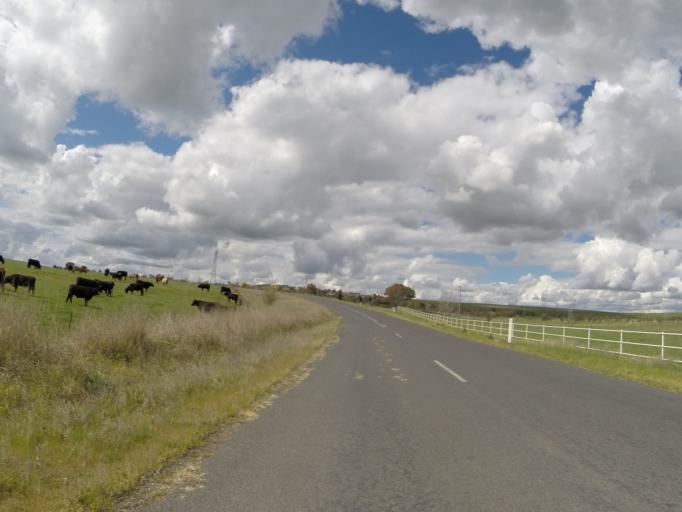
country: AU
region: New South Wales
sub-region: Yass Valley
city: Yass
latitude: -34.8737
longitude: 148.9096
